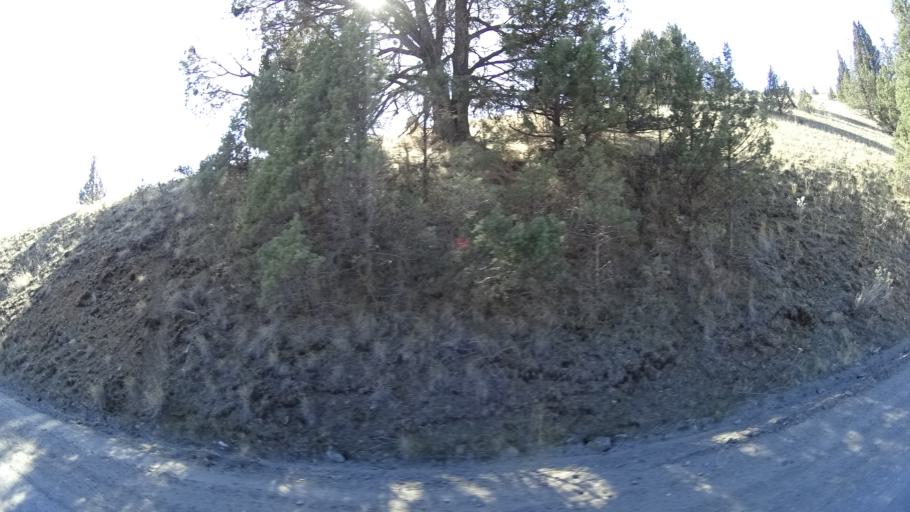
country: US
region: California
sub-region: Siskiyou County
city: Yreka
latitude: 41.7805
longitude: -122.5971
